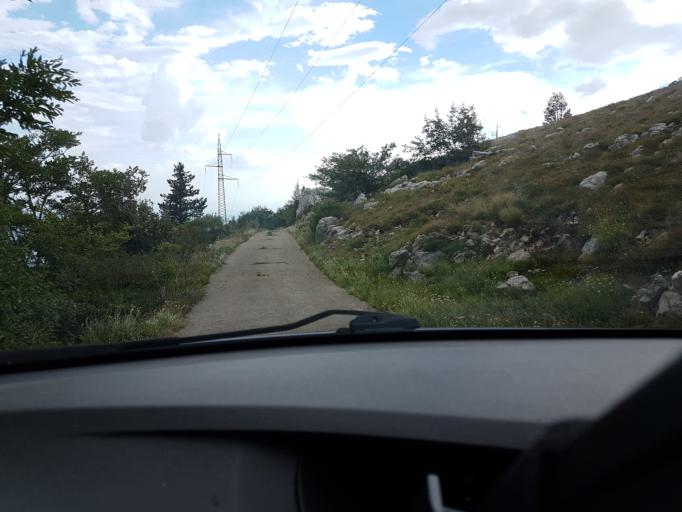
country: HR
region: Primorsko-Goranska
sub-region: Grad Crikvenica
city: Crikvenica
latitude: 45.2427
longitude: 14.6886
